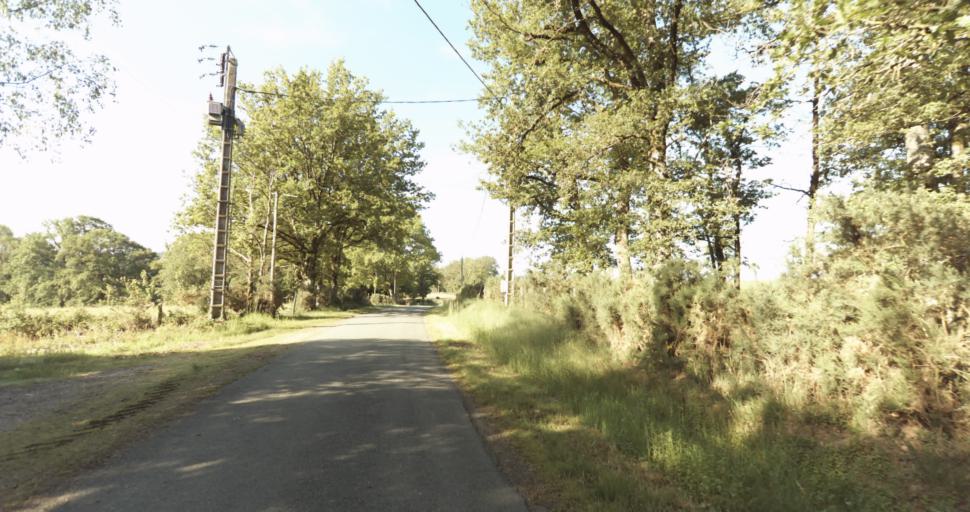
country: FR
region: Limousin
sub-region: Departement de la Haute-Vienne
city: Solignac
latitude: 45.7367
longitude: 1.2624
